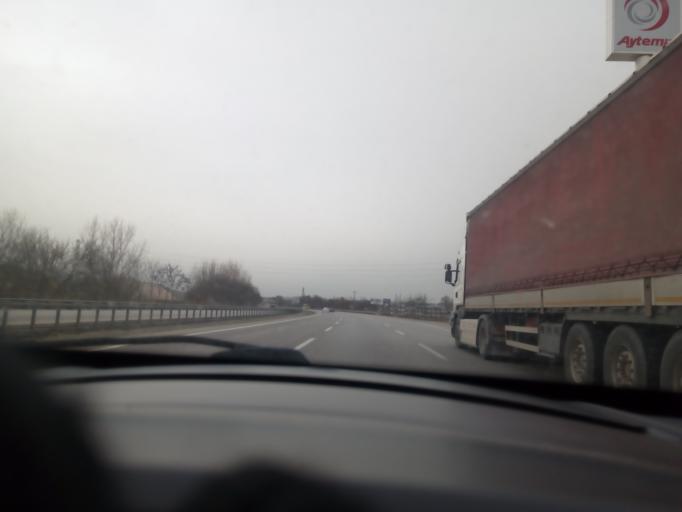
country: TR
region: Balikesir
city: Susurluk
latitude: 39.9658
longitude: 28.1708
